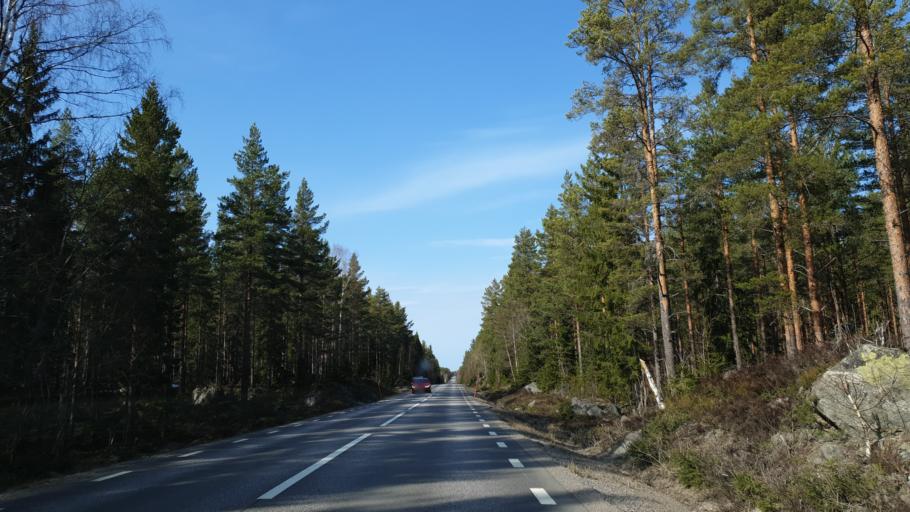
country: SE
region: Gaevleborg
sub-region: Gavle Kommun
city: Norrsundet
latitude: 61.0573
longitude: 17.1413
